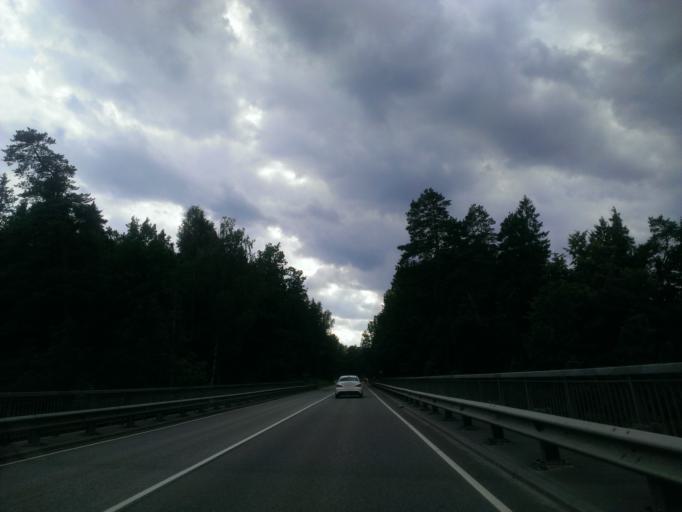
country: LV
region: Sigulda
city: Sigulda
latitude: 57.1347
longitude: 24.8052
